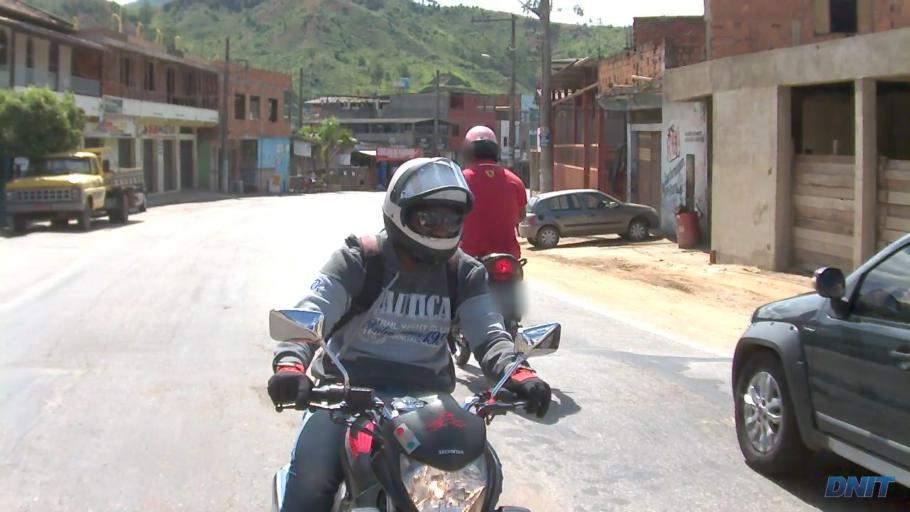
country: BR
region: Minas Gerais
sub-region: Coronel Fabriciano
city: Coronel Fabriciano
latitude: -19.5337
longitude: -42.6680
